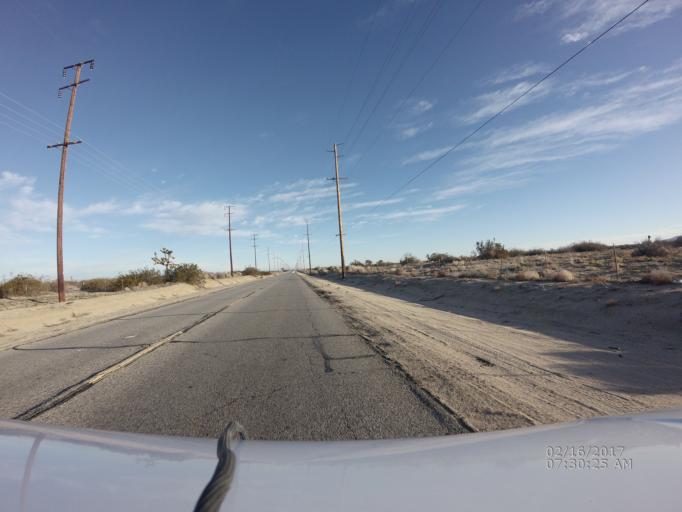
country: US
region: California
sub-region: Los Angeles County
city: Littlerock
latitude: 34.6207
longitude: -117.9695
